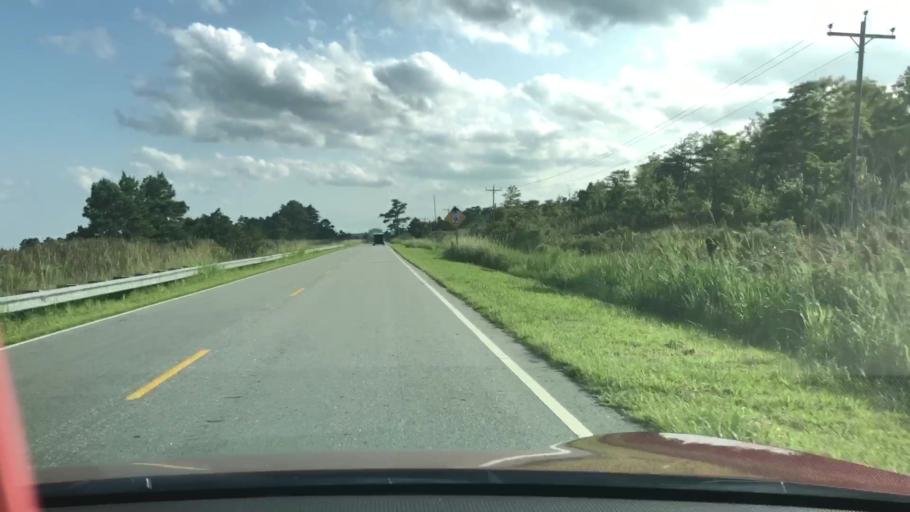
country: US
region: North Carolina
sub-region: Dare County
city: Wanchese
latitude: 35.7038
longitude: -75.7700
